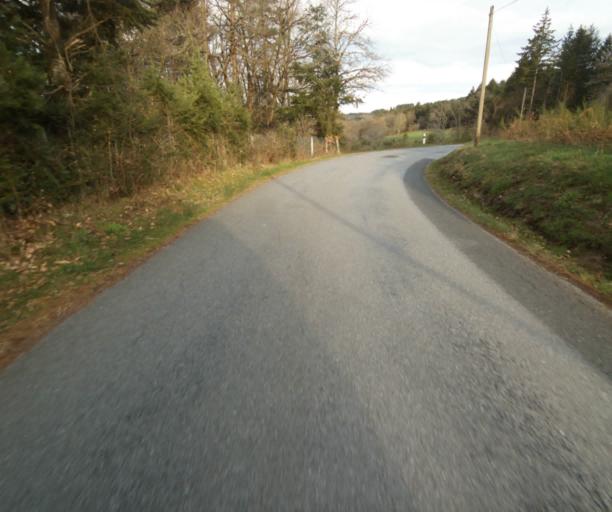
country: FR
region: Limousin
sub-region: Departement de la Correze
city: Correze
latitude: 45.4169
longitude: 1.8912
